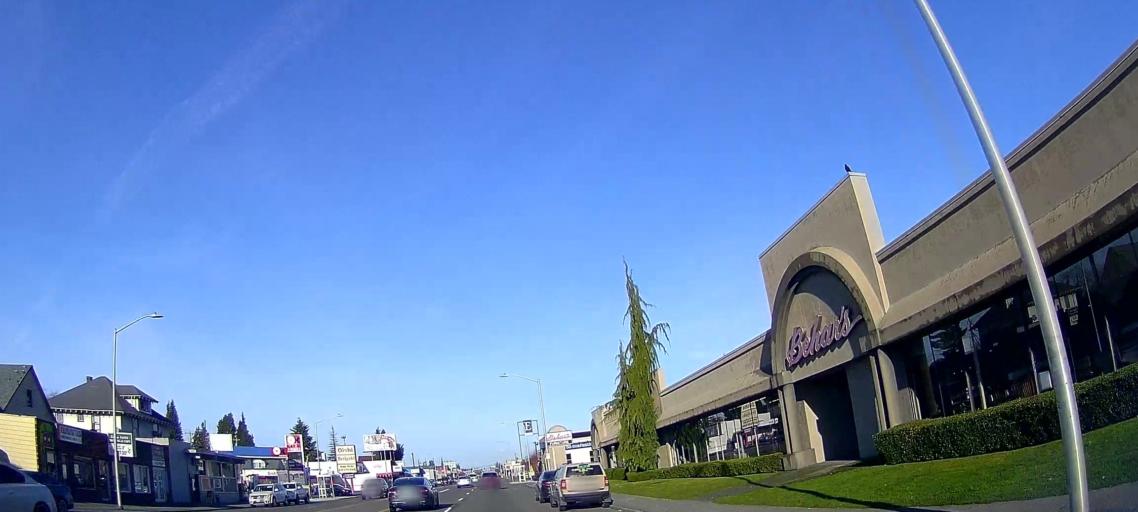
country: US
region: Washington
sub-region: Snohomish County
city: Everett
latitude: 47.9891
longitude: -122.2013
